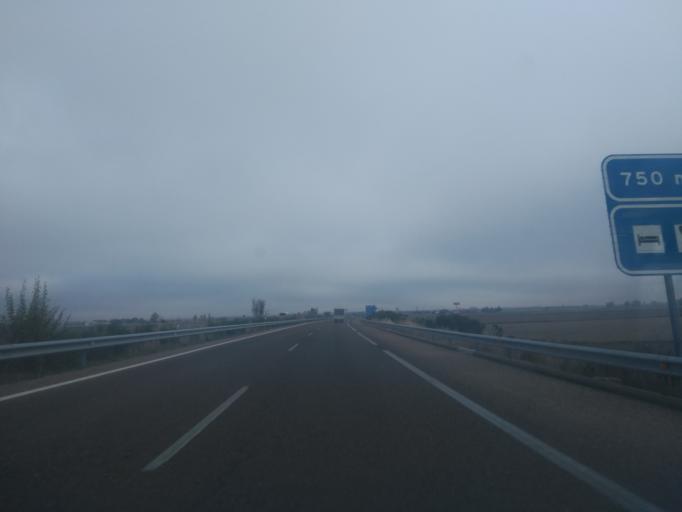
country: ES
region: Castille and Leon
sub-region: Provincia de Salamanca
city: Pedrosillo el Ralo
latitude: 41.0485
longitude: -5.5546
